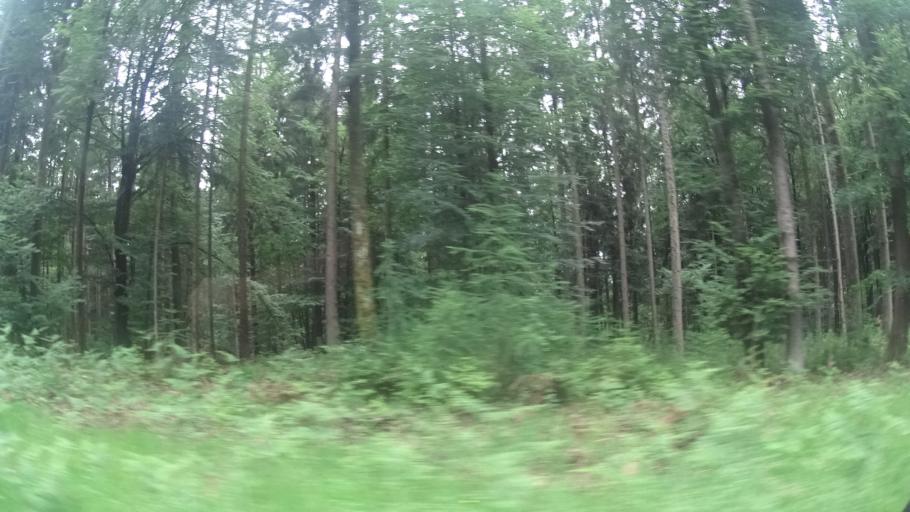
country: DE
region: Hesse
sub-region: Regierungsbezirk Darmstadt
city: Steinau an der Strasse
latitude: 50.2405
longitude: 9.4563
